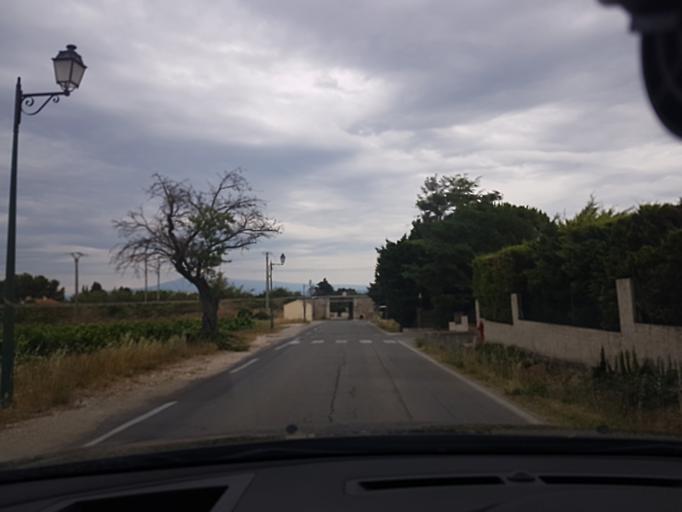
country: FR
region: Provence-Alpes-Cote d'Azur
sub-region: Departement du Vaucluse
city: Jonquerettes
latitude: 43.9486
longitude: 4.9377
